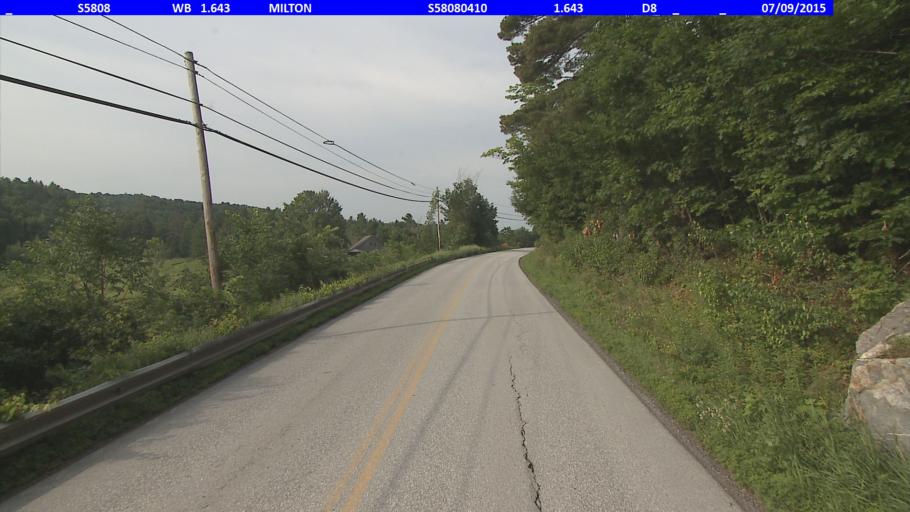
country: US
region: Vermont
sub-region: Chittenden County
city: Milton
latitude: 44.6385
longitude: -73.0832
